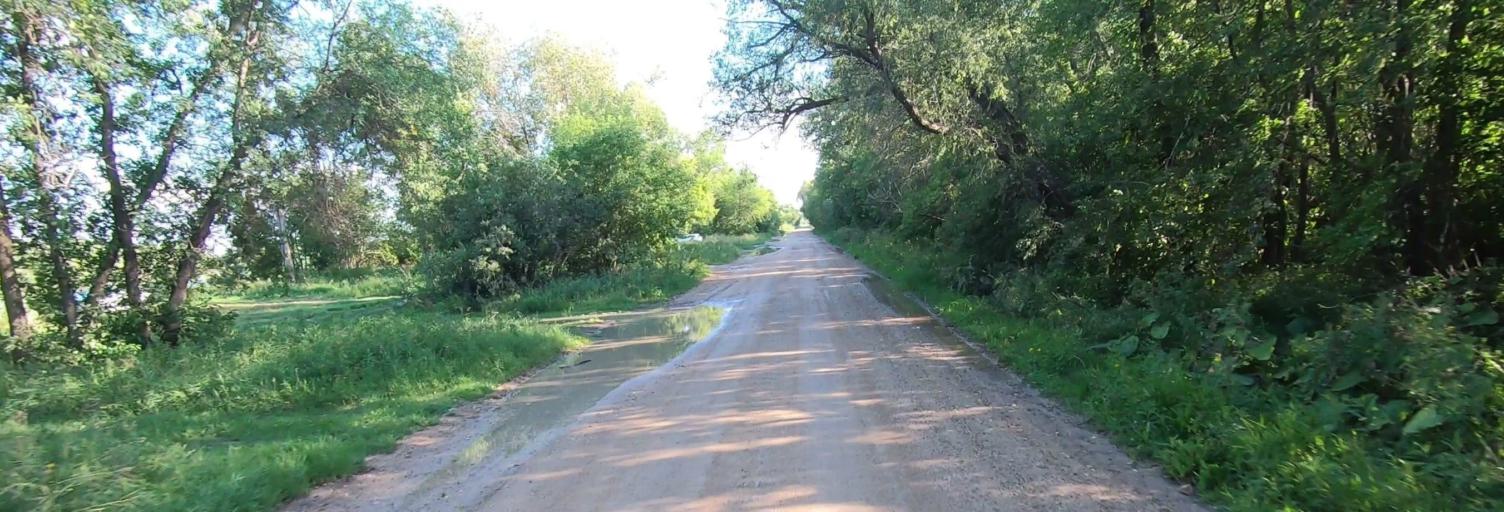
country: CA
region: Manitoba
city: Selkirk
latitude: 50.2668
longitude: -96.8494
